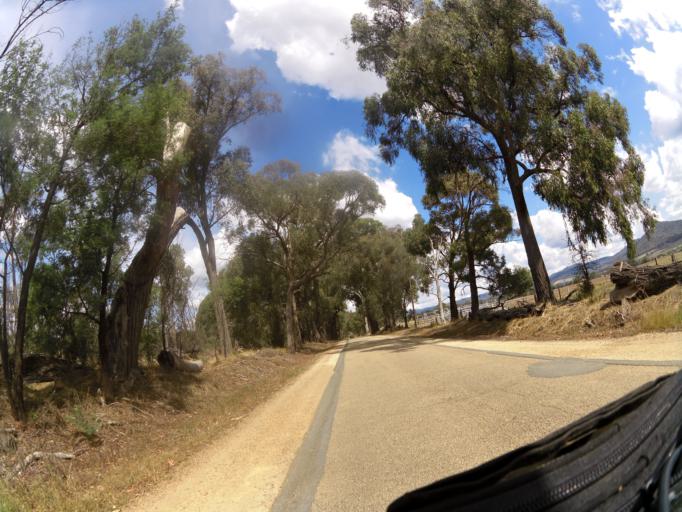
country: AU
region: Victoria
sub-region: Benalla
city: Benalla
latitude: -36.7699
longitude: 145.9752
